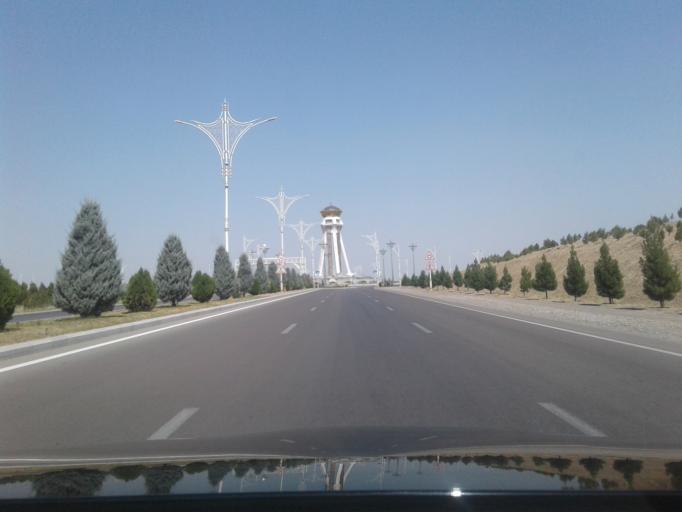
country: TM
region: Ahal
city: Ashgabat
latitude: 37.8780
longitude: 58.4192
